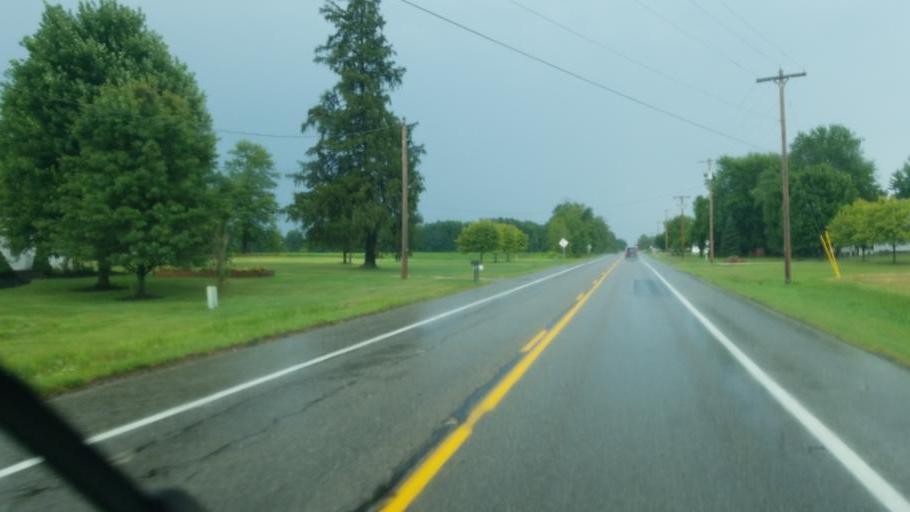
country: US
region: Ohio
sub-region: Ashtabula County
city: Orwell
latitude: 41.4617
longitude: -80.8843
